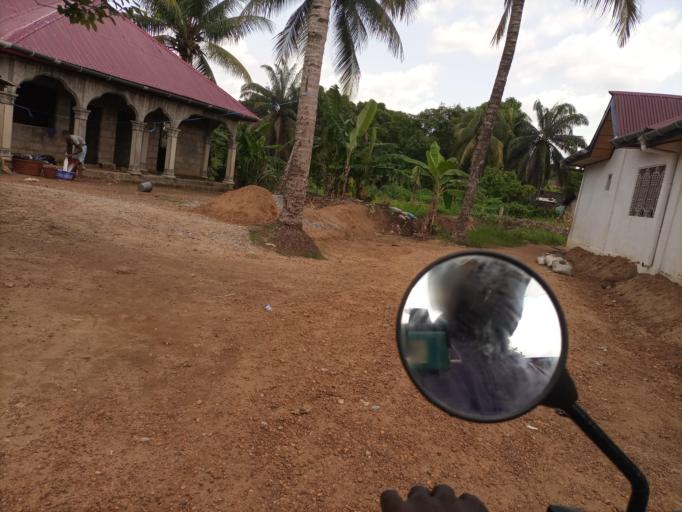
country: SL
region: Southern Province
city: Bo
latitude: 7.9478
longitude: -11.7342
